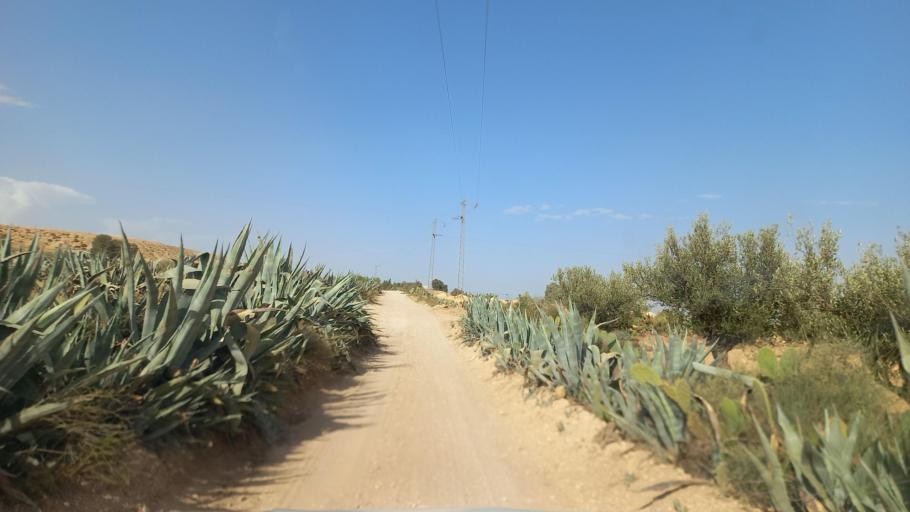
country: TN
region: Al Qasrayn
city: Kasserine
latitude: 35.2537
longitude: 8.9318
